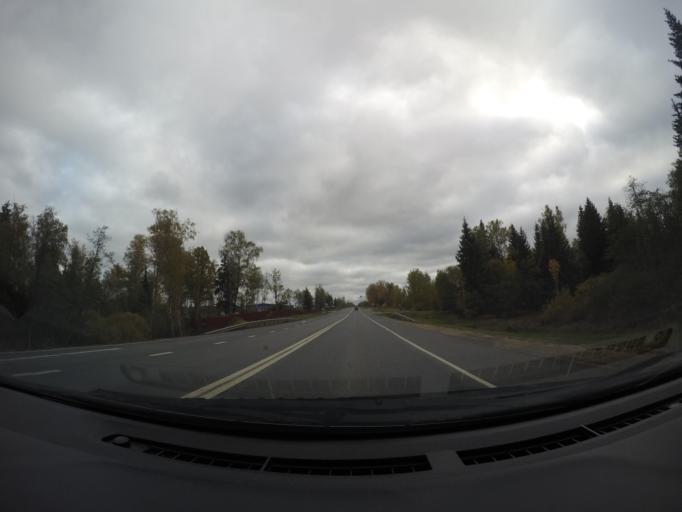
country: RU
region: Moskovskaya
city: Dorokhovo
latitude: 55.5991
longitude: 36.3599
